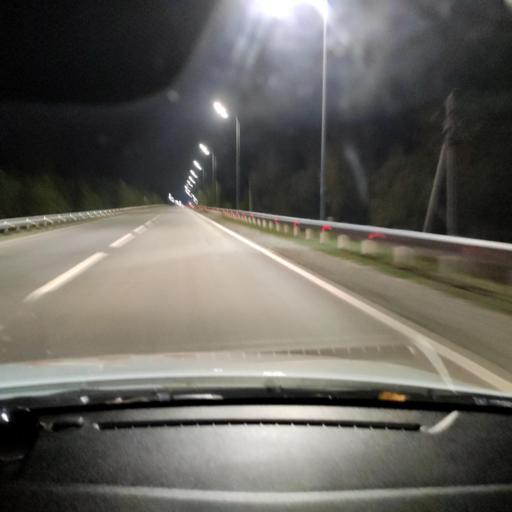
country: RU
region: Tatarstan
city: Stolbishchi
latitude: 55.6359
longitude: 49.1069
